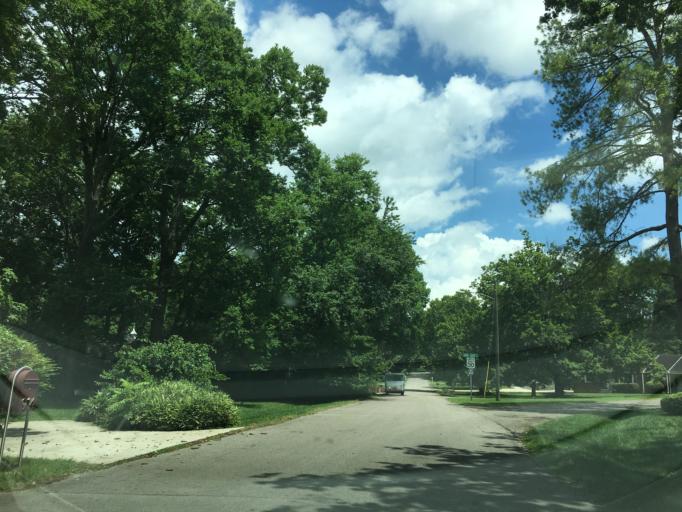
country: US
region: Tennessee
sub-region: Davidson County
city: Oak Hill
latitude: 36.0963
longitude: -86.7897
